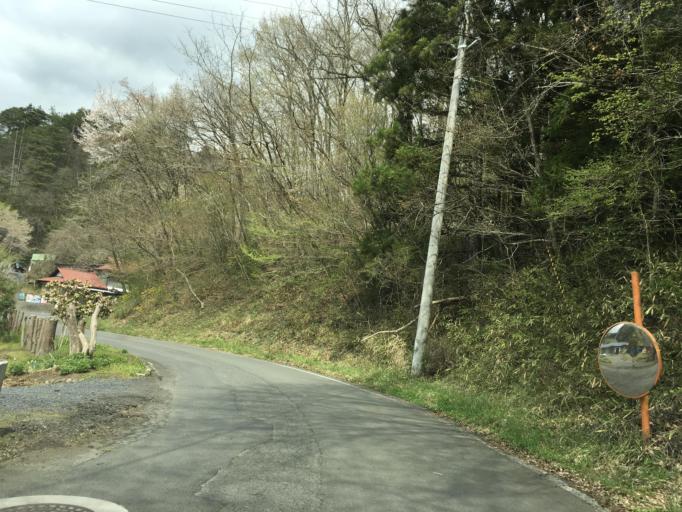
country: JP
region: Iwate
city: Ichinoseki
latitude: 38.8558
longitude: 141.3088
